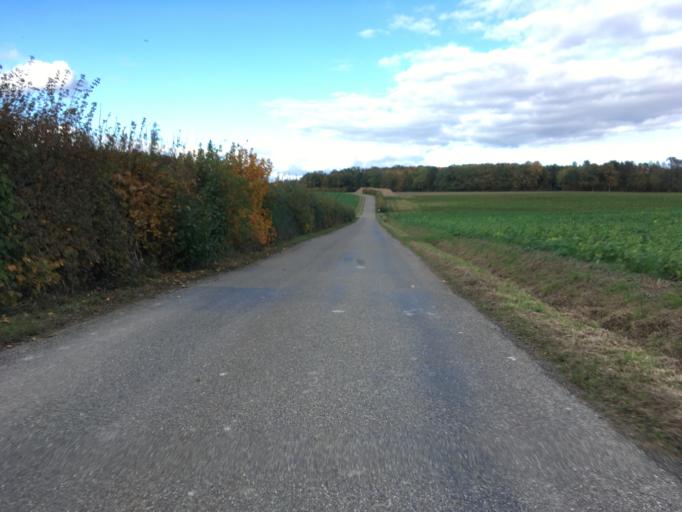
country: DE
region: Baden-Wuerttemberg
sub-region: Regierungsbezirk Stuttgart
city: Kupferzell
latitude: 49.2425
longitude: 9.7434
